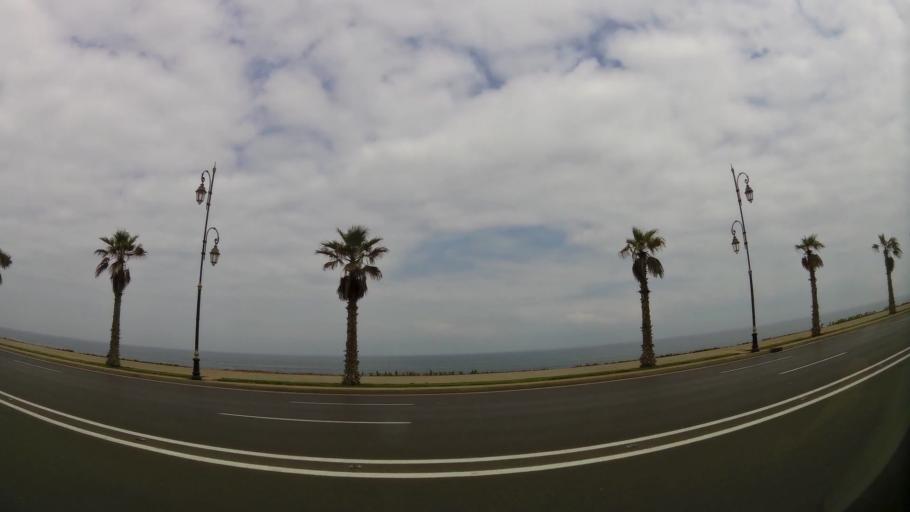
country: MA
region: Rabat-Sale-Zemmour-Zaer
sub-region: Rabat
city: Rabat
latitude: 34.0040
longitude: -6.8714
